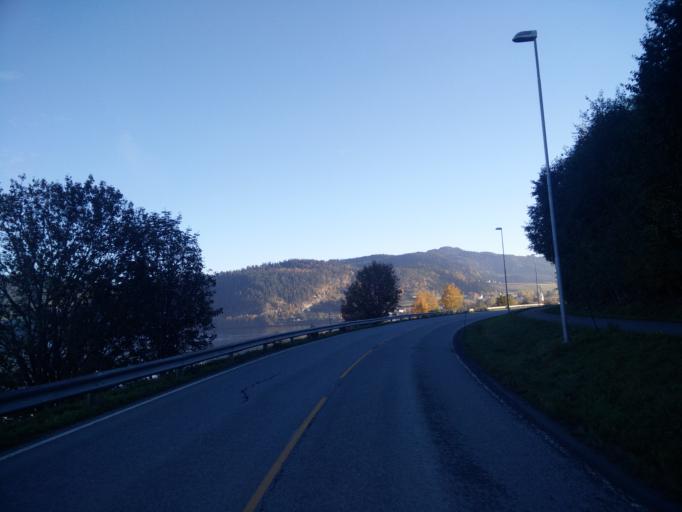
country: NO
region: Sor-Trondelag
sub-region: Skaun
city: Borsa
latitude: 63.3321
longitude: 10.0691
